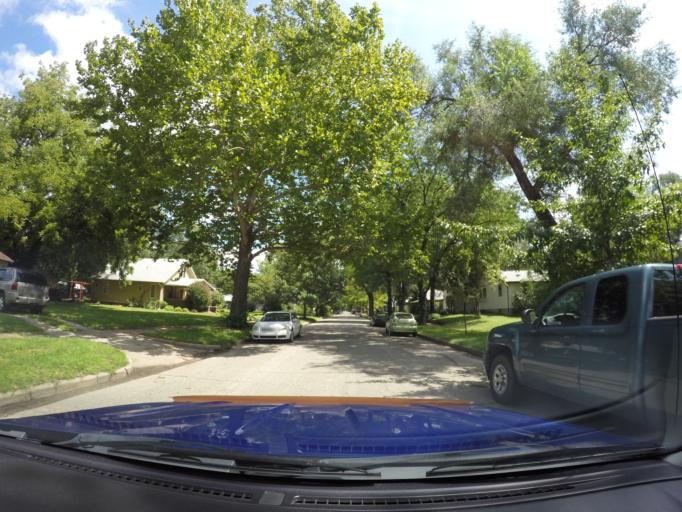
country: US
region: Kansas
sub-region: Riley County
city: Manhattan
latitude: 39.1763
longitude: -96.5763
